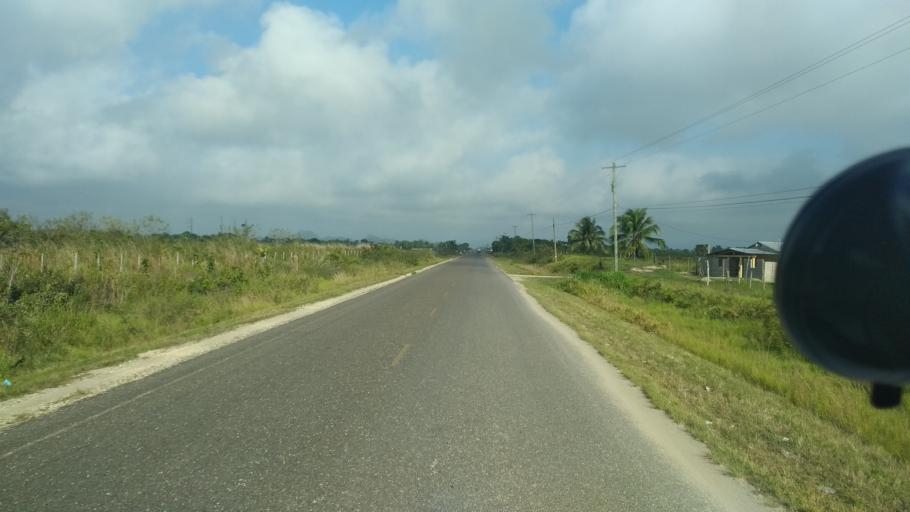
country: BZ
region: Stann Creek
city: Placencia
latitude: 16.5098
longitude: -88.5384
